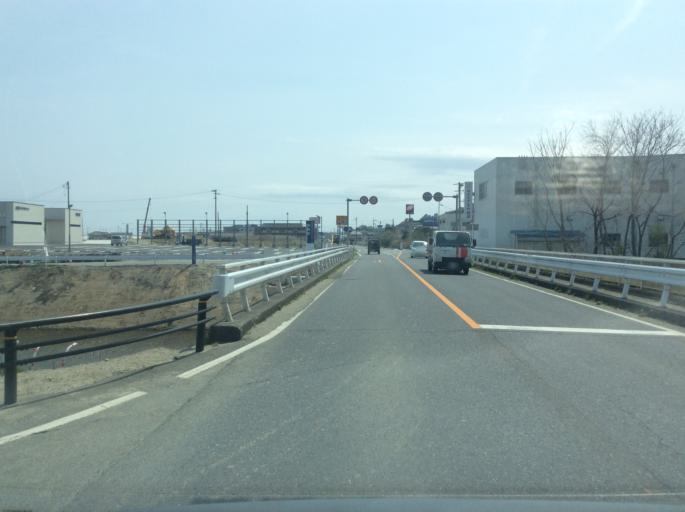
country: JP
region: Fukushima
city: Iwaki
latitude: 37.1475
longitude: 140.9957
